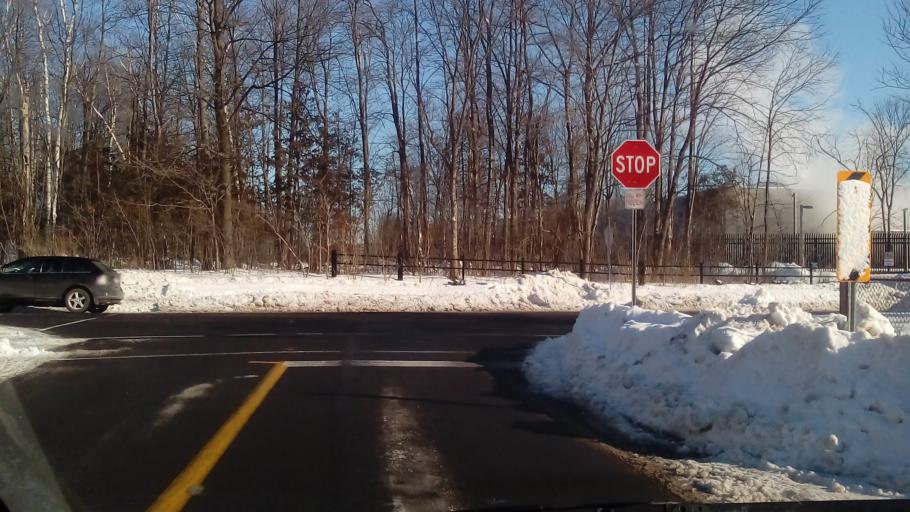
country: CA
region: Ontario
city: Ottawa
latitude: 45.4369
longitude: -75.6203
